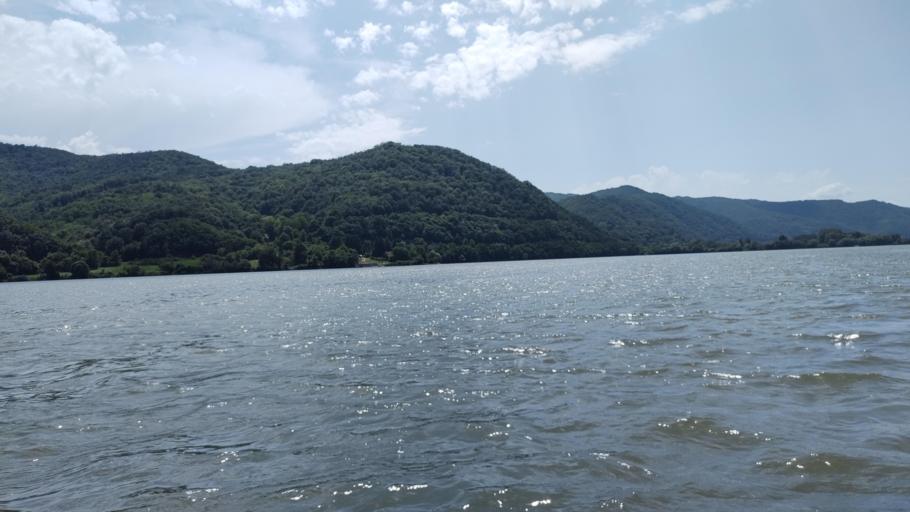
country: RO
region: Caras-Severin
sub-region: Comuna Berzasca
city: Liubcova
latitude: 44.6515
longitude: 21.8602
